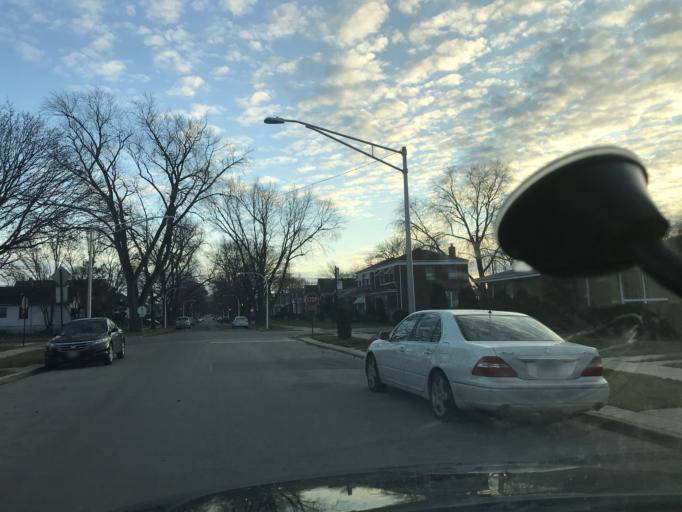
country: US
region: Illinois
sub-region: Cook County
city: Burnham
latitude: 41.7357
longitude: -87.5769
